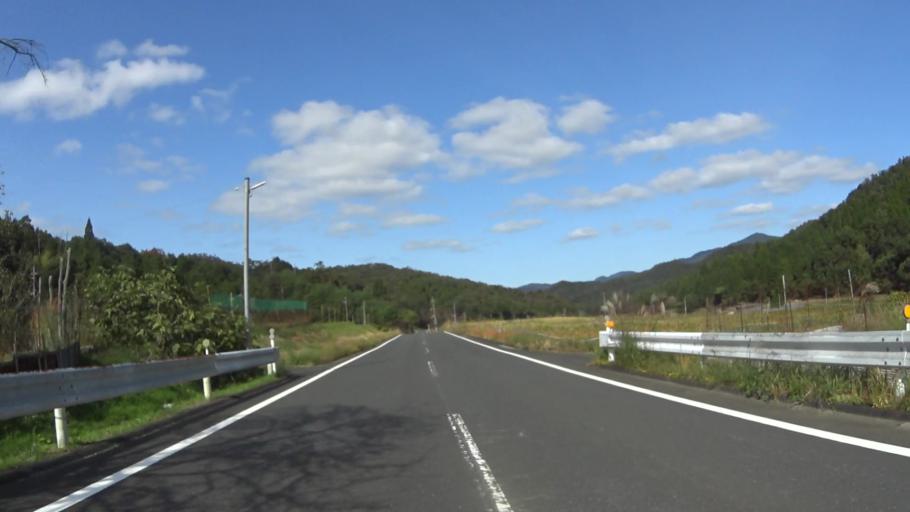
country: JP
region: Hyogo
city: Toyooka
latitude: 35.5497
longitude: 134.9775
